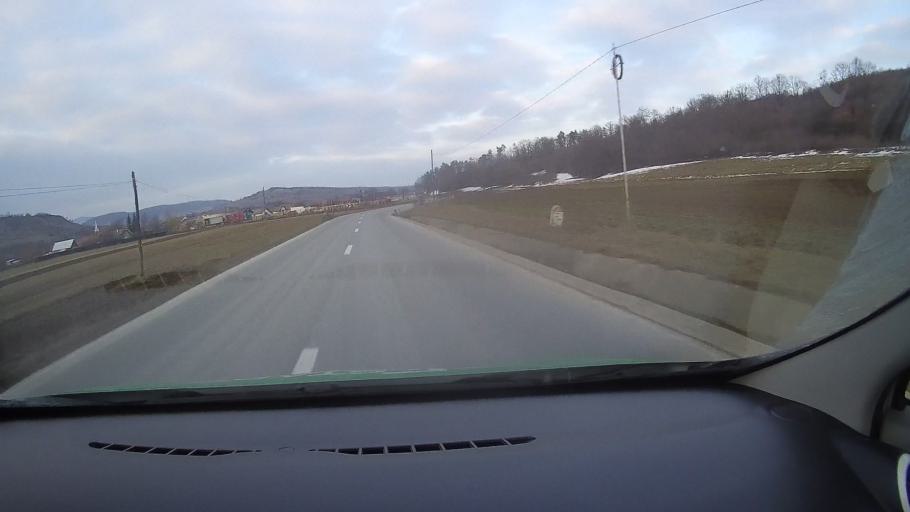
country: RO
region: Harghita
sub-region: Comuna Simonesti
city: Simonesti
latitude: 46.3498
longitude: 25.1275
